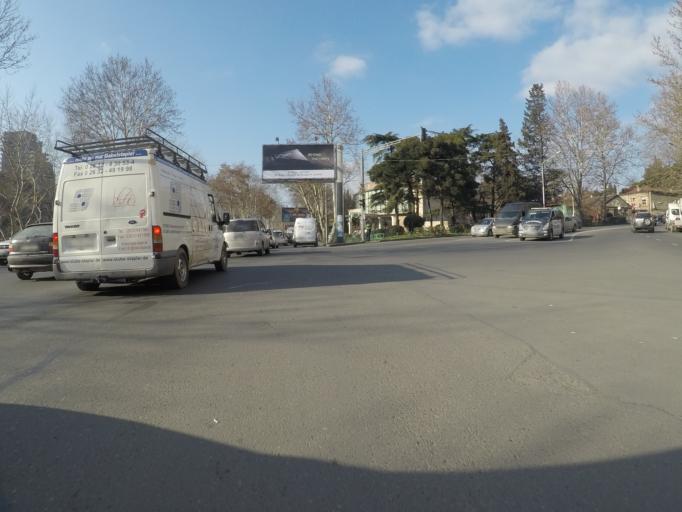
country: GE
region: T'bilisi
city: Tbilisi
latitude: 41.7196
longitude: 44.7863
